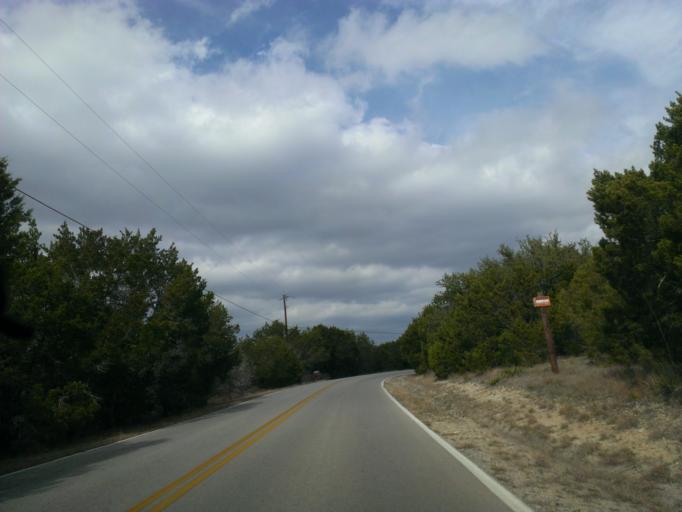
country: US
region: Texas
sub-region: Travis County
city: Briarcliff
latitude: 30.3737
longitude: -98.0864
